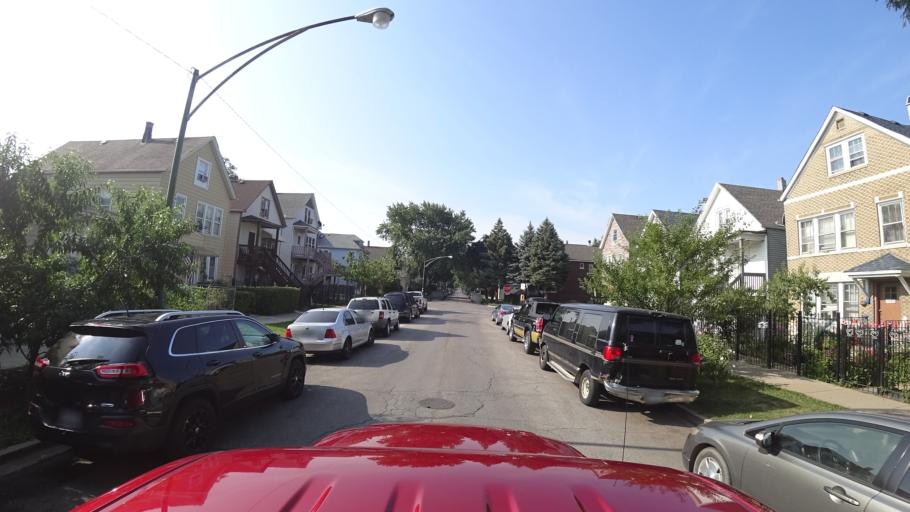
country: US
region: Illinois
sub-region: Cook County
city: Chicago
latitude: 41.8141
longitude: -87.6956
